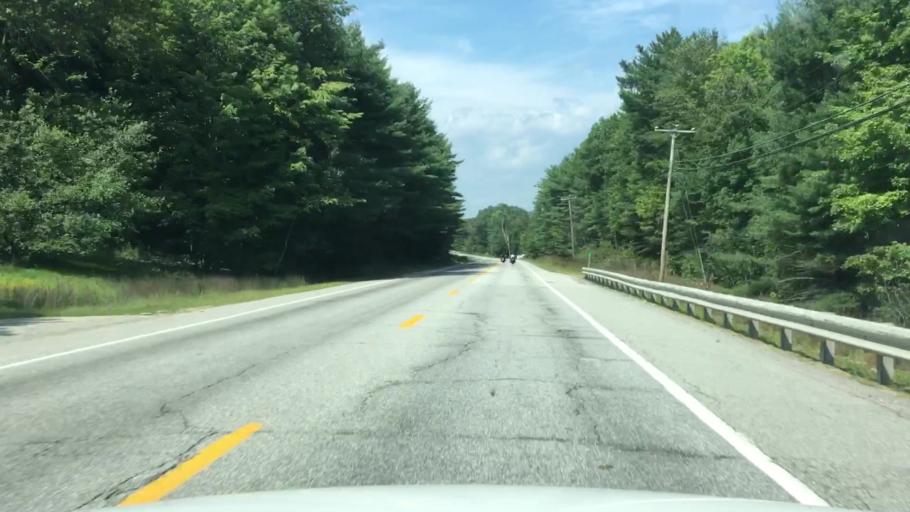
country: US
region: Maine
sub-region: Oxford County
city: Peru
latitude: 44.4927
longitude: -70.3852
